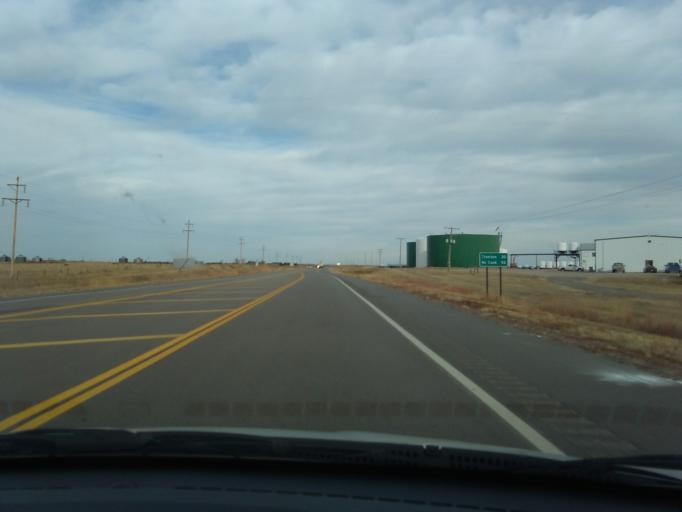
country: US
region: Nebraska
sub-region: Dundy County
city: Benkelman
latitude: 40.0626
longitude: -101.5301
